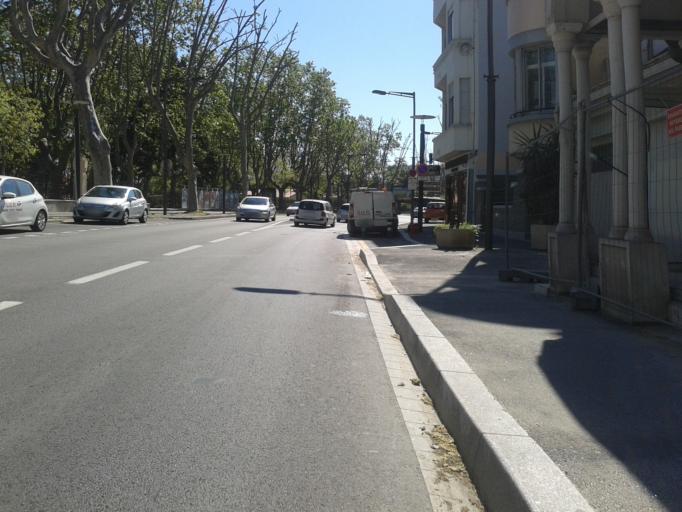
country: FR
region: Languedoc-Roussillon
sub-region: Departement des Pyrenees-Orientales
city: Perpignan
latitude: 42.7011
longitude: 2.9016
